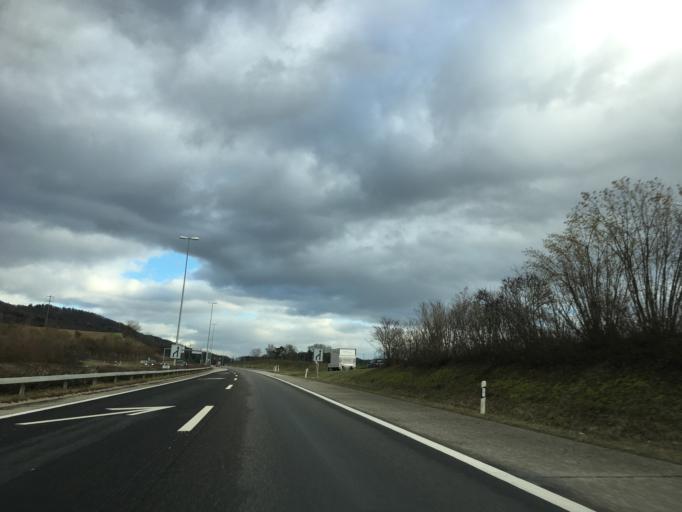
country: CH
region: Zurich
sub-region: Bezirk Buelach
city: Glattfelden
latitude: 47.5578
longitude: 8.5139
